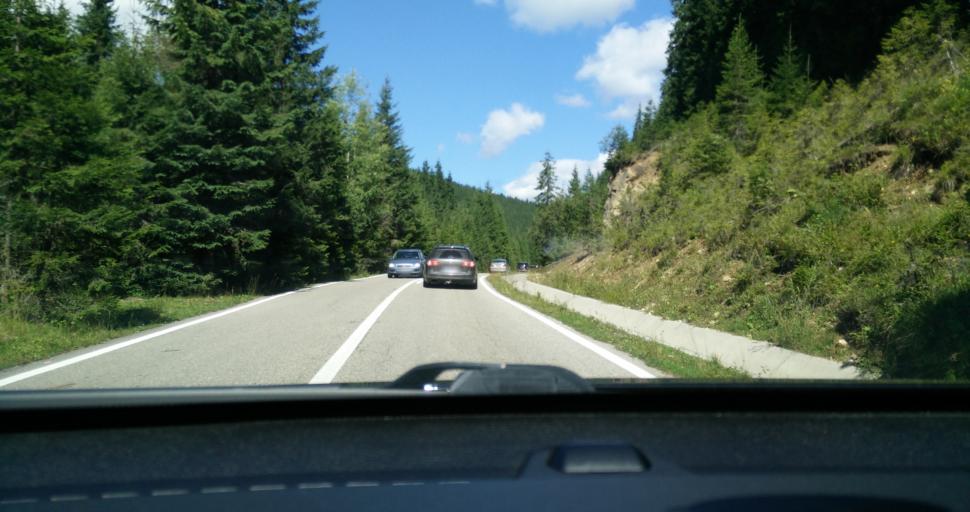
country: RO
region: Alba
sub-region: Comuna Sugag
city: Sugag
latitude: 45.5328
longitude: 23.6427
